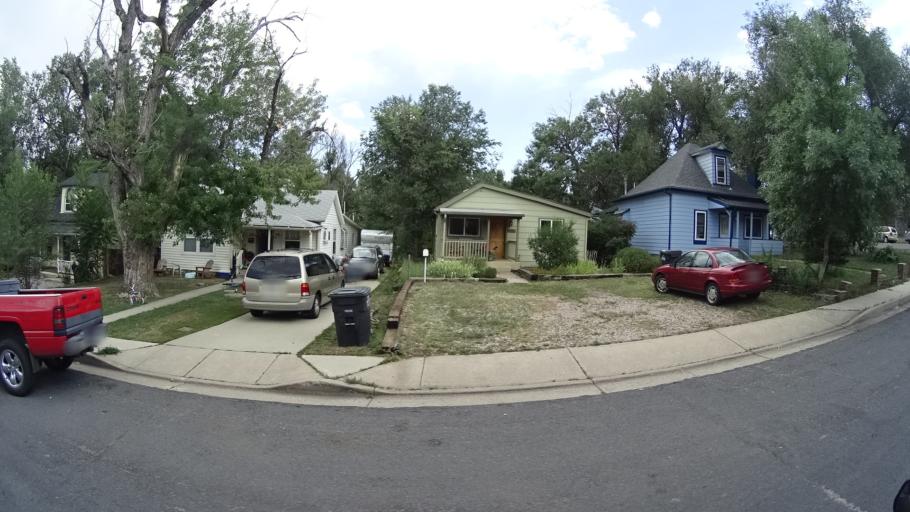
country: US
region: Colorado
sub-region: El Paso County
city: Colorado Springs
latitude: 38.8296
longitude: -104.8082
